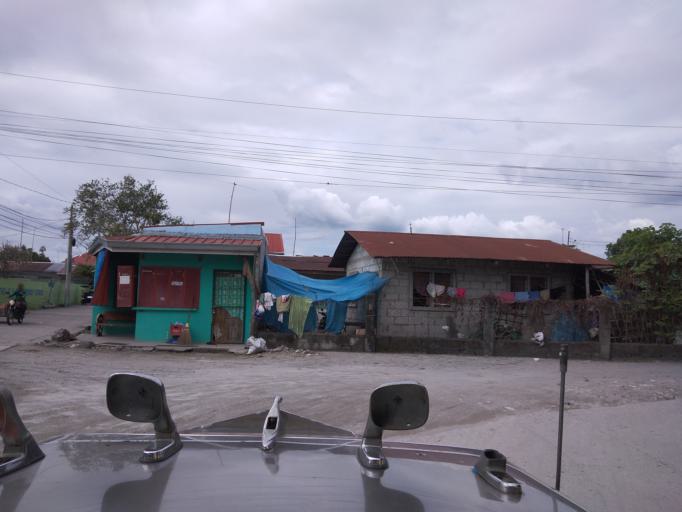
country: PH
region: Central Luzon
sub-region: Province of Pampanga
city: Pandacaqui
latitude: 15.1811
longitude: 120.6476
